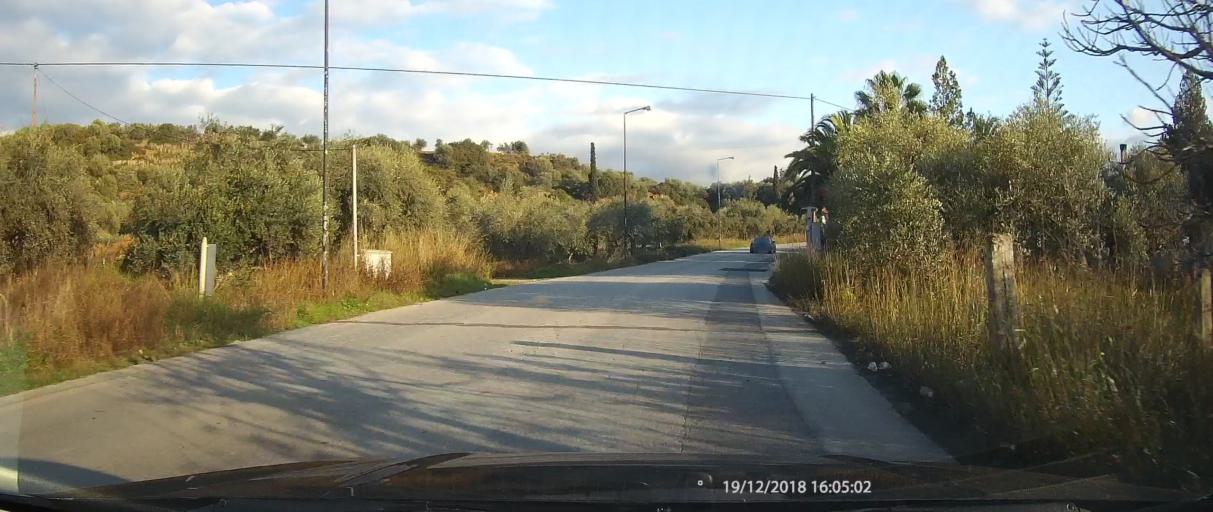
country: GR
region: Peloponnese
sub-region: Nomos Lakonias
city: Vlakhiotis
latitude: 36.8627
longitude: 22.7170
